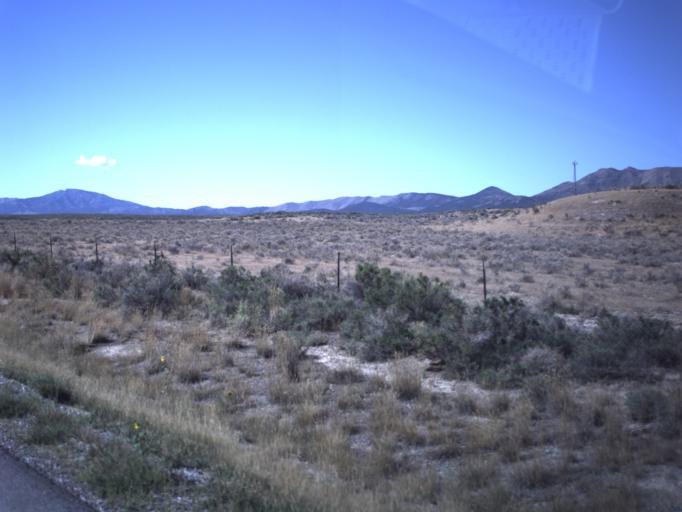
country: US
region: Utah
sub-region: Tooele County
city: Tooele
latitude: 40.2048
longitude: -112.4103
